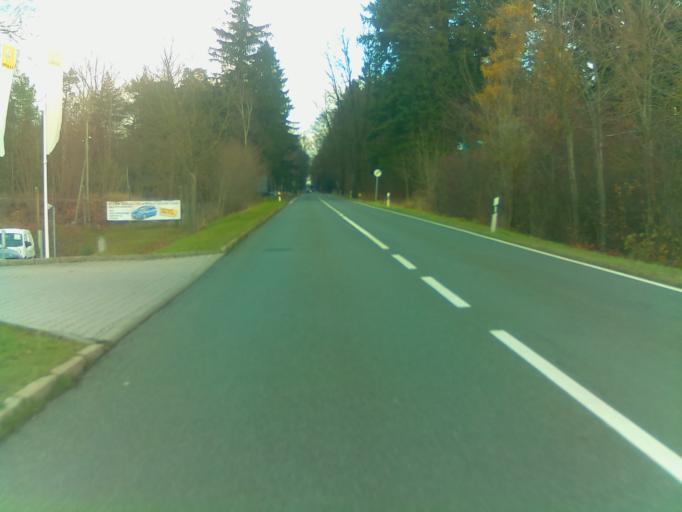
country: DE
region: Thuringia
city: Hildburghausen
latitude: 50.4429
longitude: 10.7351
